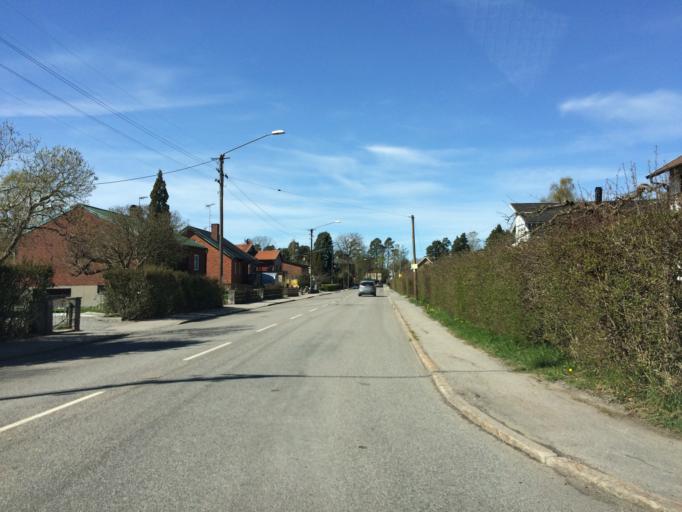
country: SE
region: Stockholm
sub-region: Huddinge Kommun
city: Huddinge
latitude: 59.2668
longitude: 17.9767
